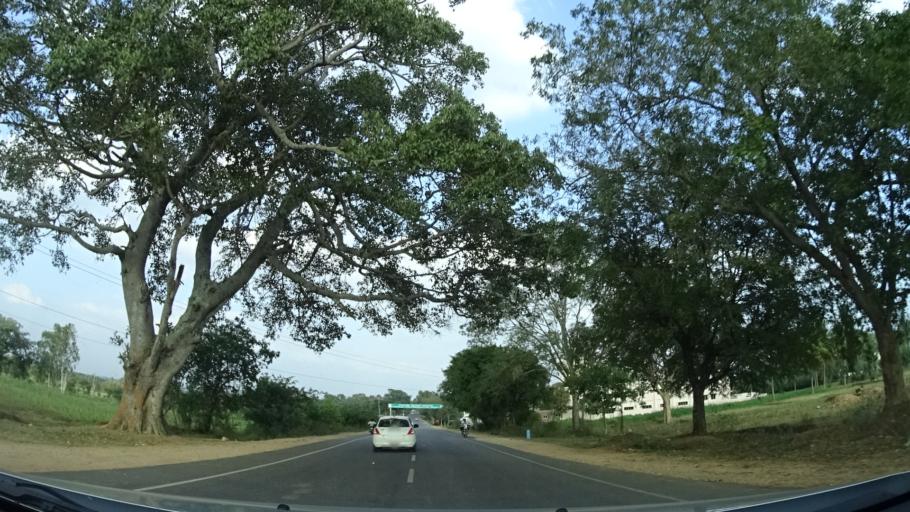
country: IN
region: Karnataka
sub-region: Mandya
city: Malavalli
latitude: 12.3745
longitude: 77.0333
